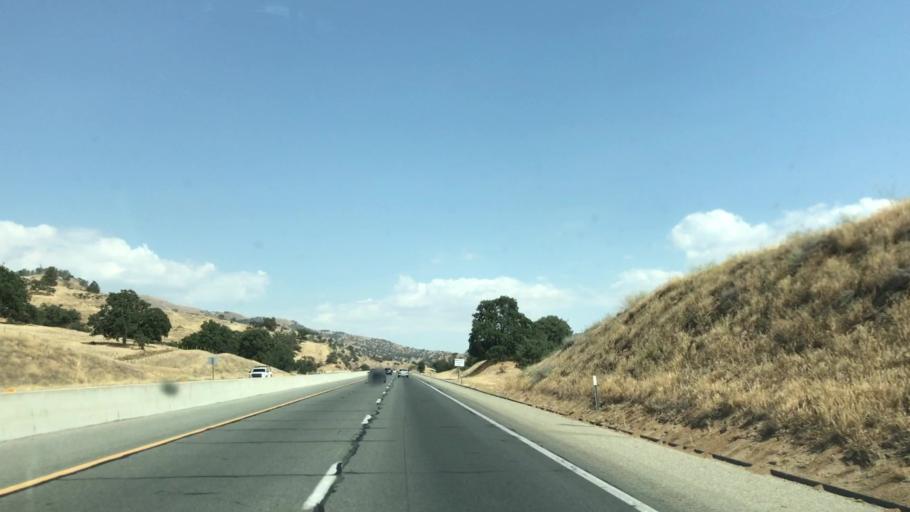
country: US
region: California
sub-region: Kern County
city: Golden Hills
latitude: 35.2116
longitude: -118.5451
